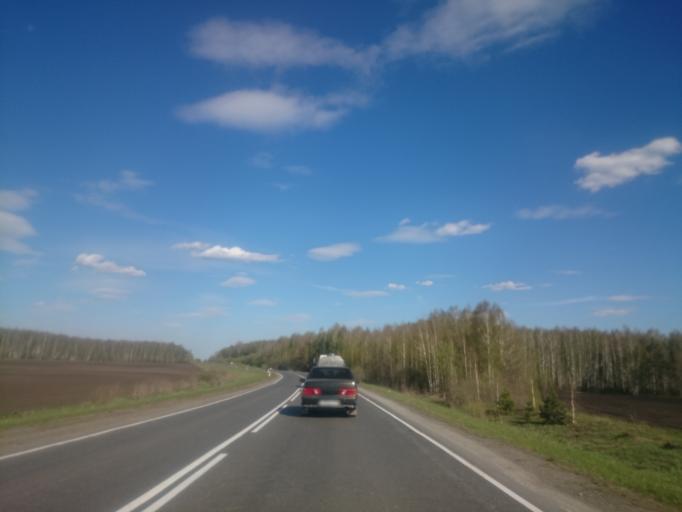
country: RU
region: Sverdlovsk
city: Lesnoy
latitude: 57.6181
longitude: 63.1809
